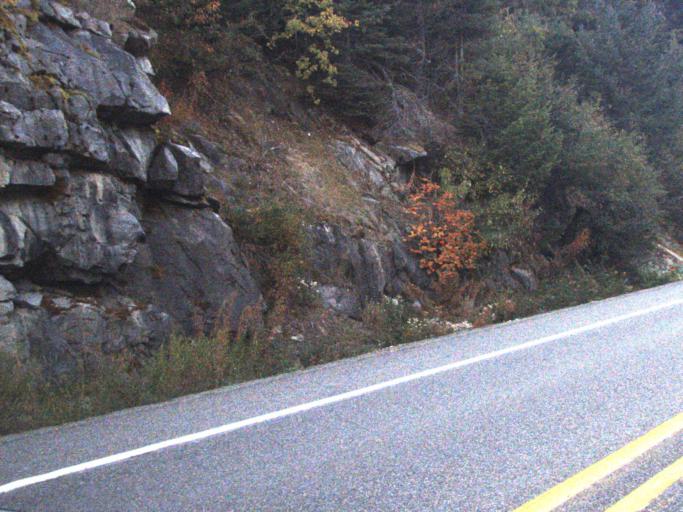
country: US
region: Washington
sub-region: Snohomish County
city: Darrington
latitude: 48.6377
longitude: -120.8507
